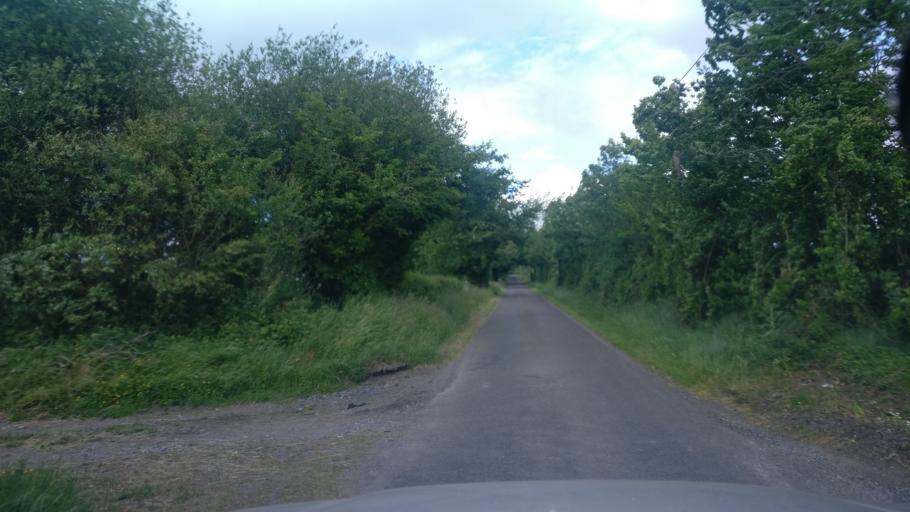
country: IE
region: Connaught
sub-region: County Galway
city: Portumna
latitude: 53.1982
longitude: -8.3636
